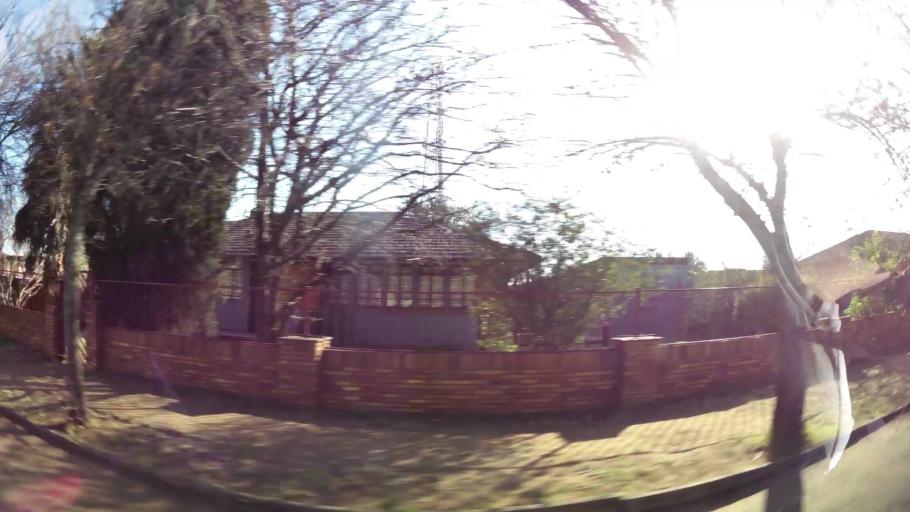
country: ZA
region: Gauteng
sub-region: West Rand District Municipality
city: Randfontein
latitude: -26.1776
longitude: 27.7063
